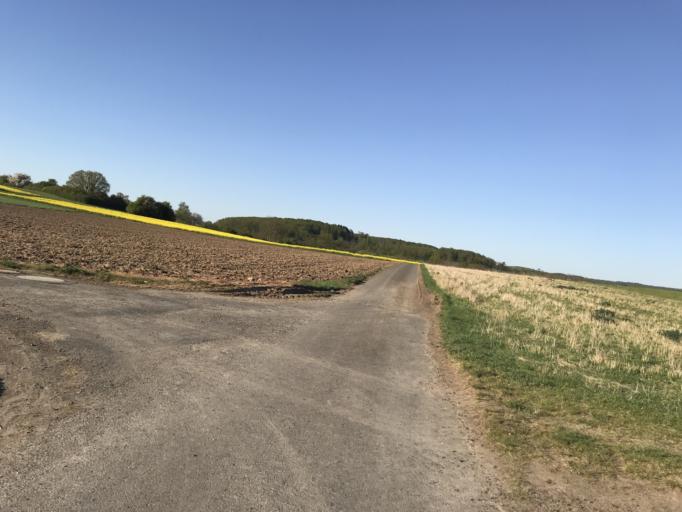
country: DE
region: Hesse
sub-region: Regierungsbezirk Giessen
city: Grossen Buseck
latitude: 50.5890
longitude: 8.8038
